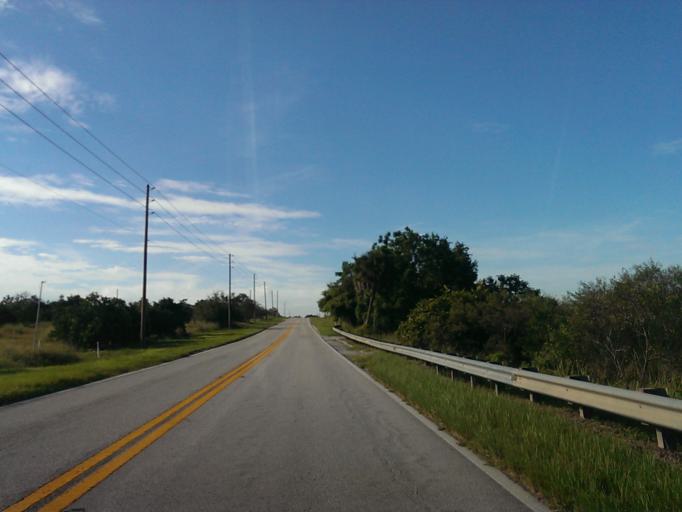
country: US
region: Florida
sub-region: Polk County
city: Citrus Ridge
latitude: 28.4148
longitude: -81.6359
